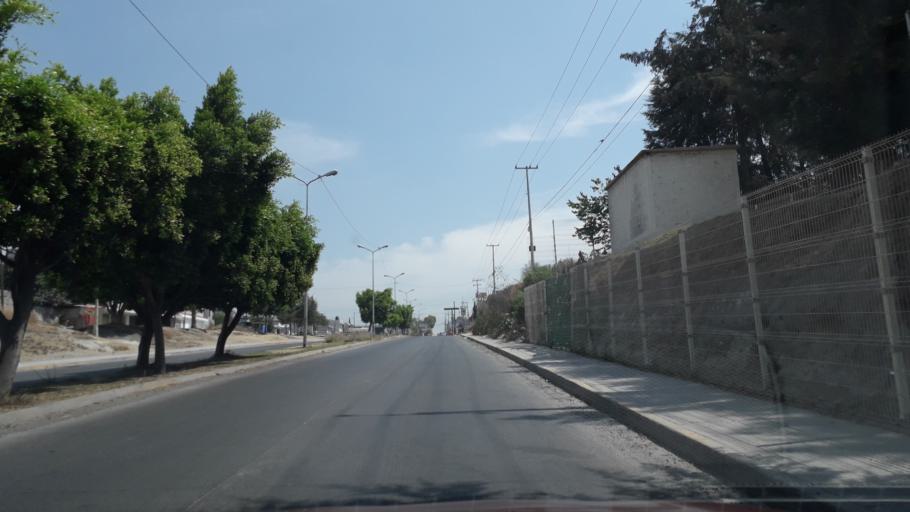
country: MX
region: Puebla
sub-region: Puebla
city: El Capulo (La Quebradora)
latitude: 18.9593
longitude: -98.2677
